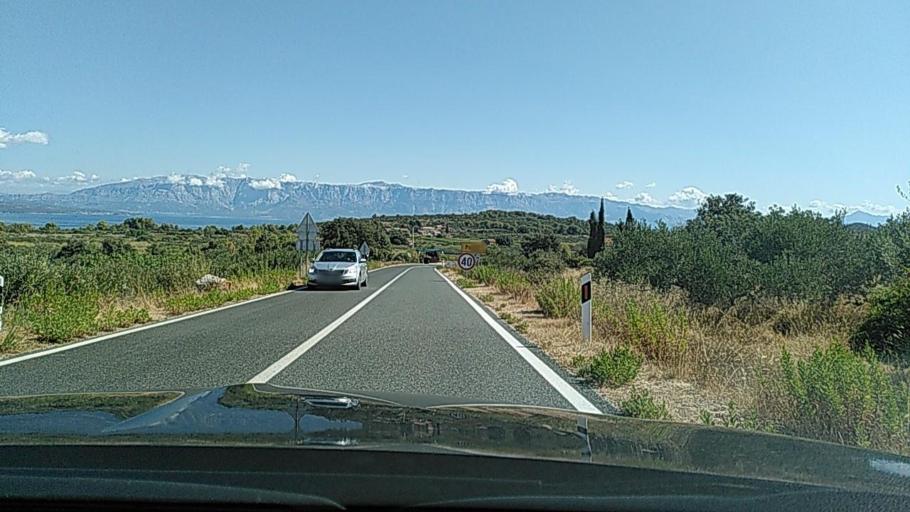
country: HR
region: Splitsko-Dalmatinska
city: Jelsa
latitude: 43.1483
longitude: 16.7889
